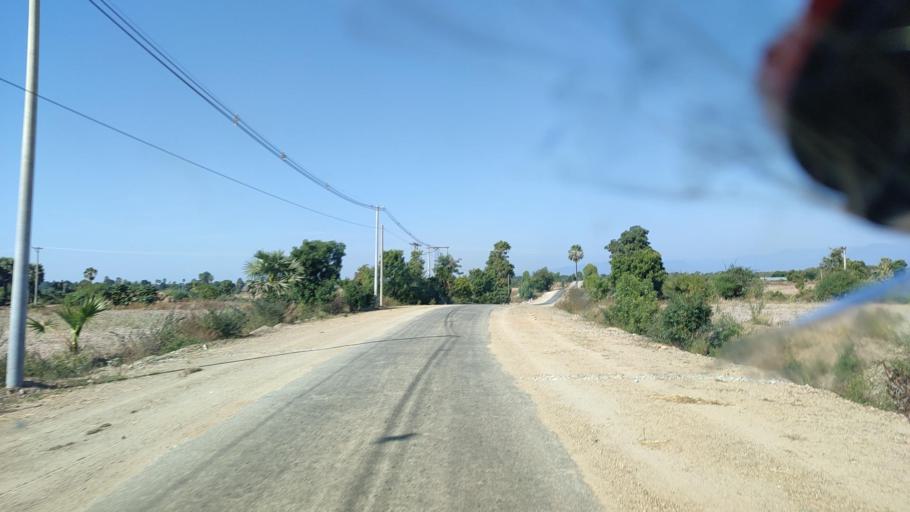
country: MM
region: Mandalay
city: Pyinmana
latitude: 20.0883
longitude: 96.2642
